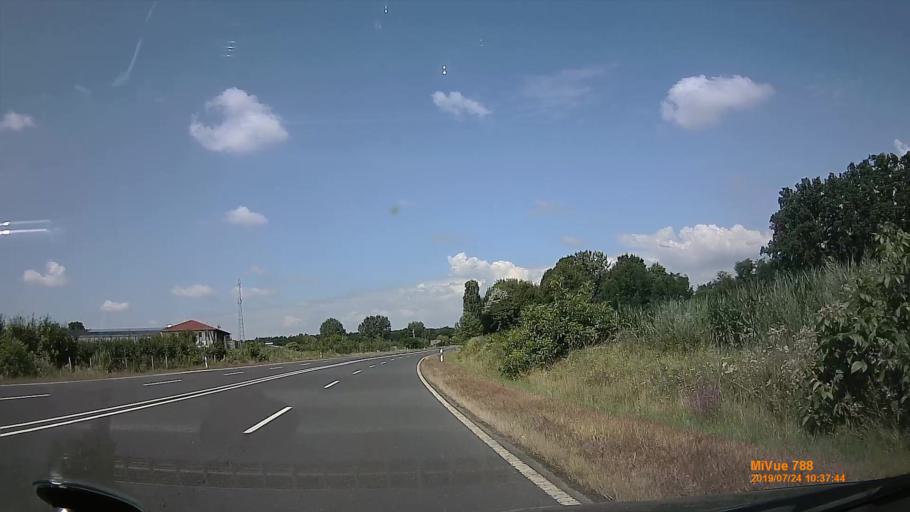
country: HU
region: Szabolcs-Szatmar-Bereg
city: Tarpa
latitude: 48.1584
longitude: 22.5533
